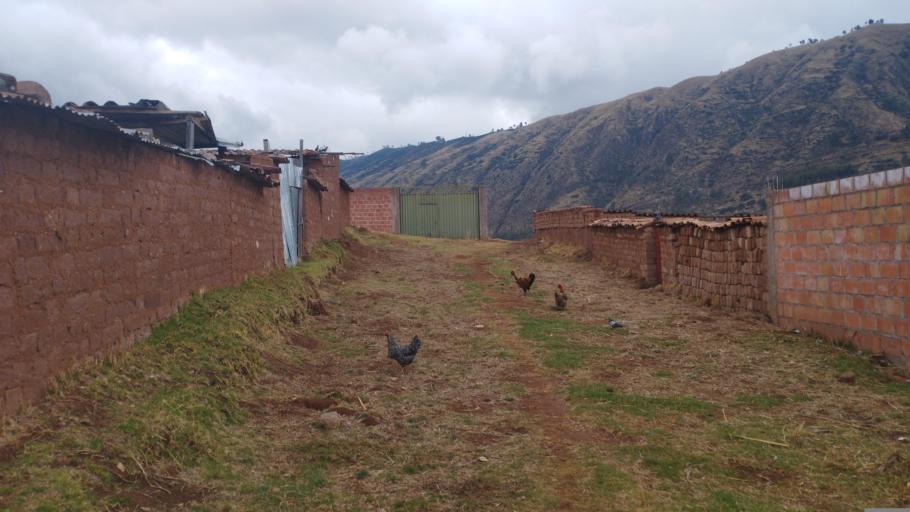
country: PE
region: Cusco
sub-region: Provincia de Cusco
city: Cusco
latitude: -13.5191
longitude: -71.9148
